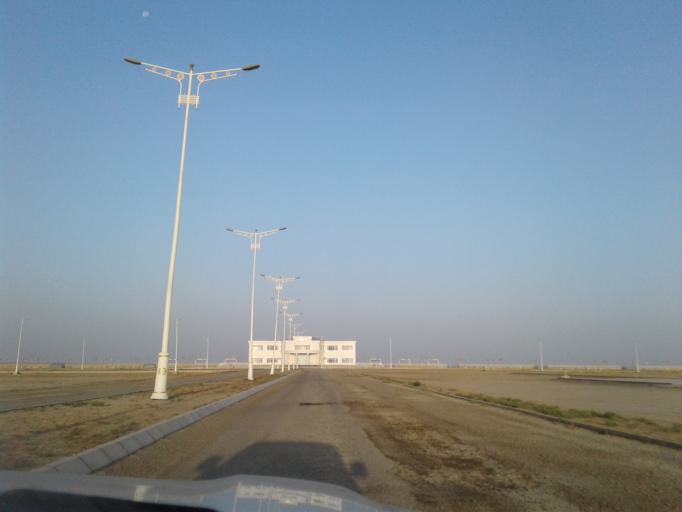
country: IR
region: Golestan
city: Aq Qayeh
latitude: 37.7057
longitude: 54.7450
